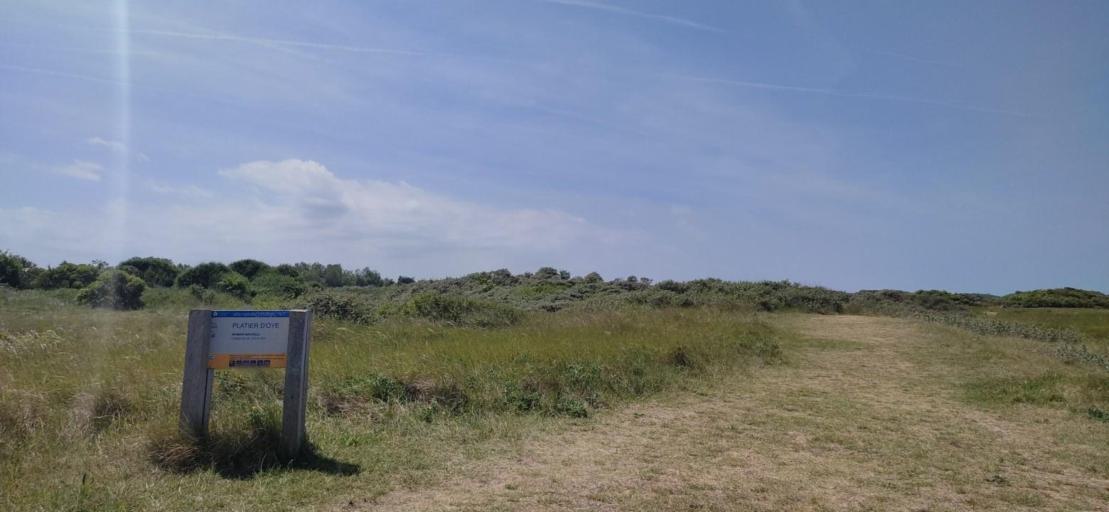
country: FR
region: Nord-Pas-de-Calais
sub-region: Departement du Nord
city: Grand-Fort-Philippe
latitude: 51.0038
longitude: 2.0894
